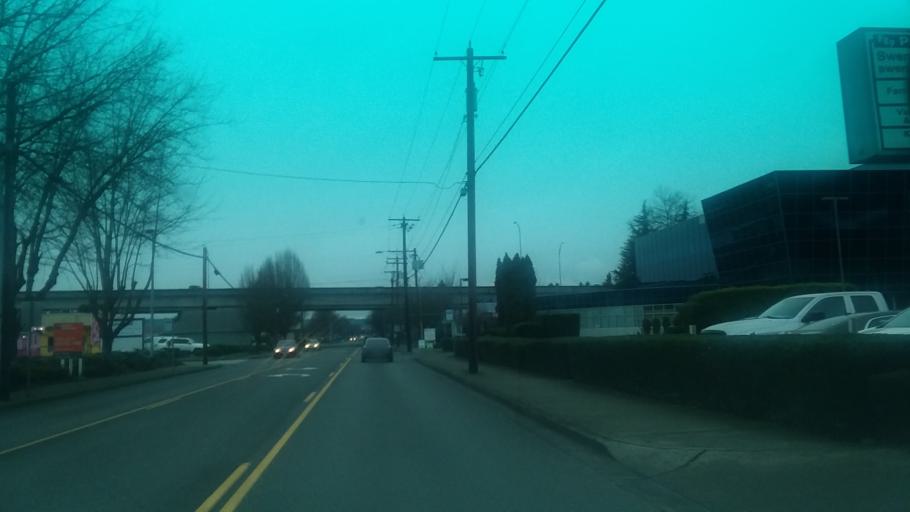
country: US
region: Washington
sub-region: Pierce County
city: Puyallup
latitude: 47.1918
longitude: -122.2805
